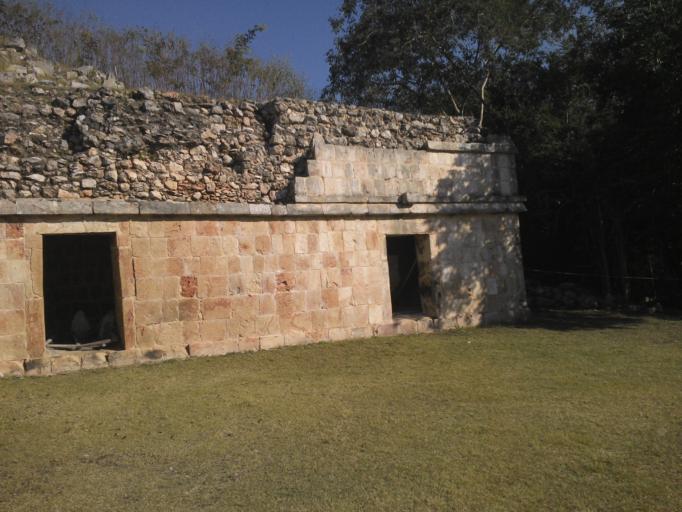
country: MX
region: Yucatan
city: Santa Elena
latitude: 20.2481
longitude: -89.6471
